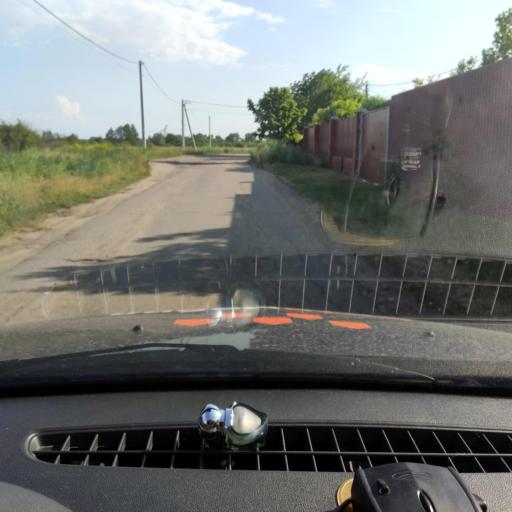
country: RU
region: Voronezj
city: Podkletnoye
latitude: 51.6192
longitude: 39.4465
